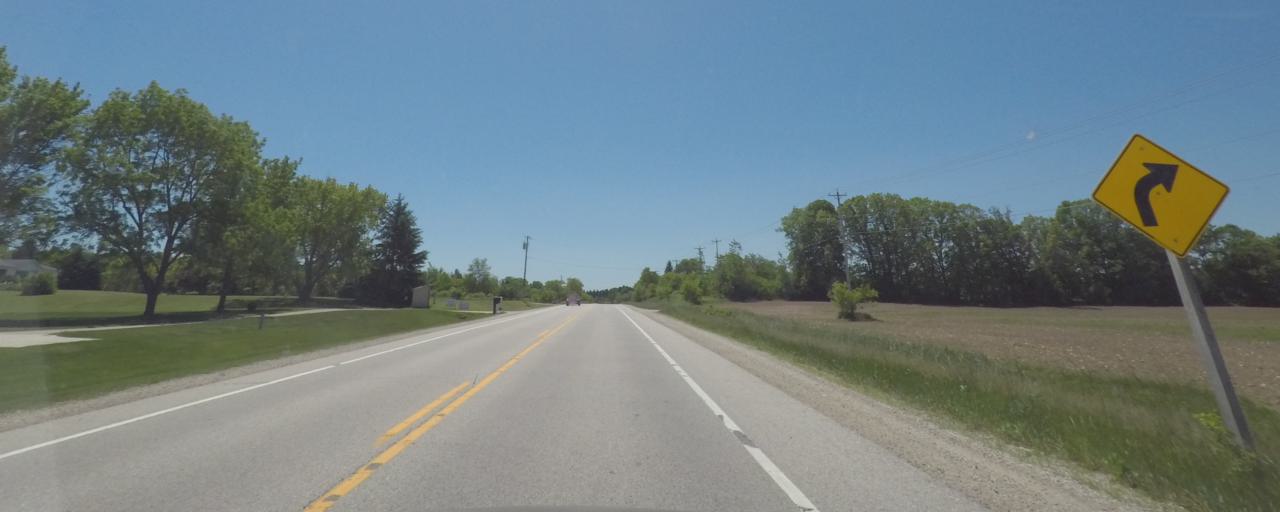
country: US
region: Wisconsin
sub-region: Ozaukee County
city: Kohler
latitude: 43.5508
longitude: -88.0778
